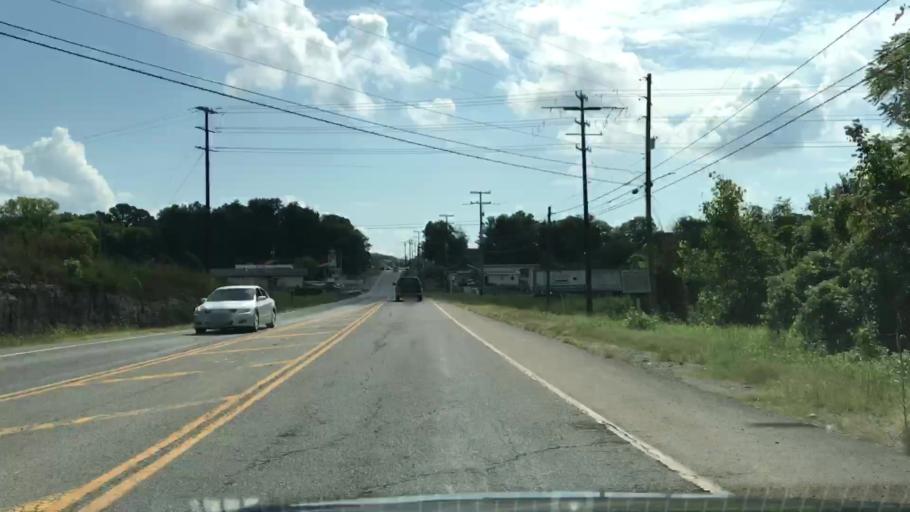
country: US
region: Tennessee
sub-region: Trousdale County
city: Hartsville
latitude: 36.4010
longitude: -86.1678
